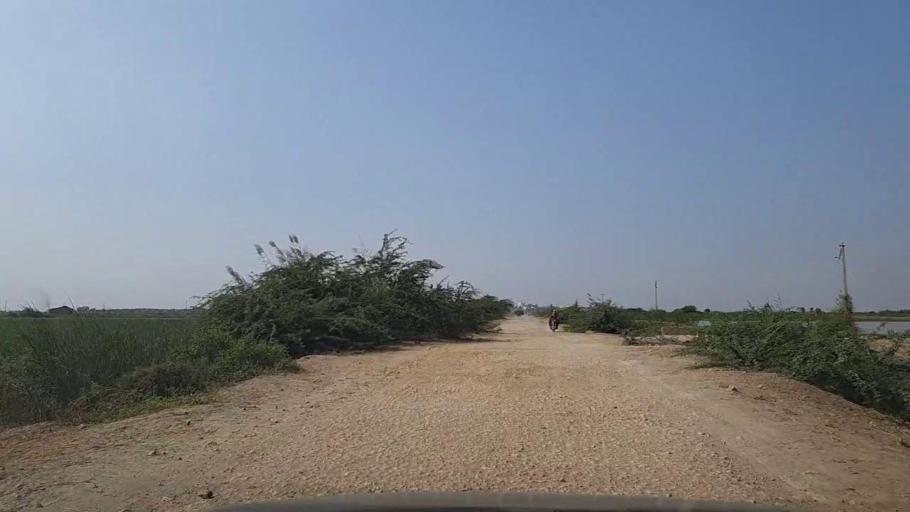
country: PK
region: Sindh
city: Chuhar Jamali
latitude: 24.5475
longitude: 67.8996
